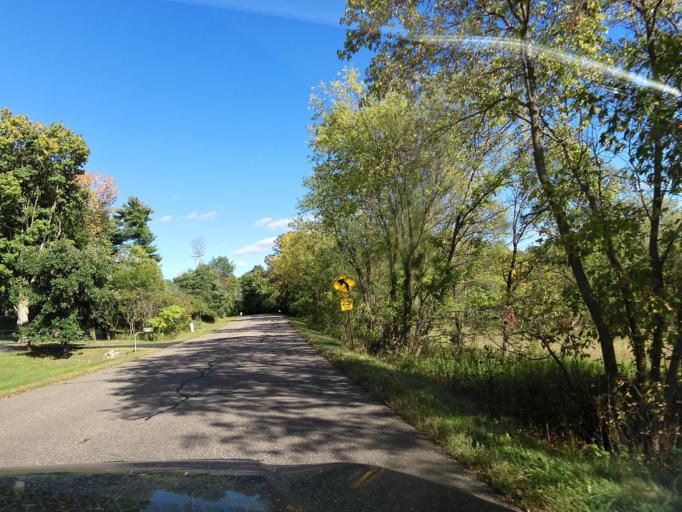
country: US
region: Minnesota
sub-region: Washington County
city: Afton
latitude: 44.8764
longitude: -92.8078
